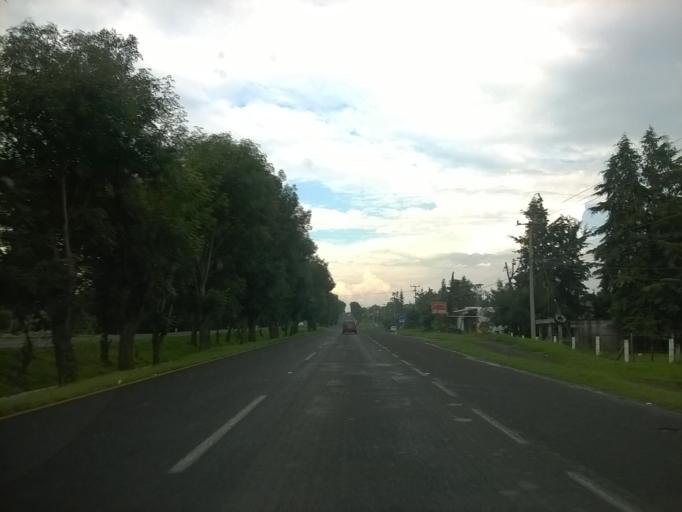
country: MX
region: Michoacan
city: Cuanajo
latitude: 19.5356
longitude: -101.5128
